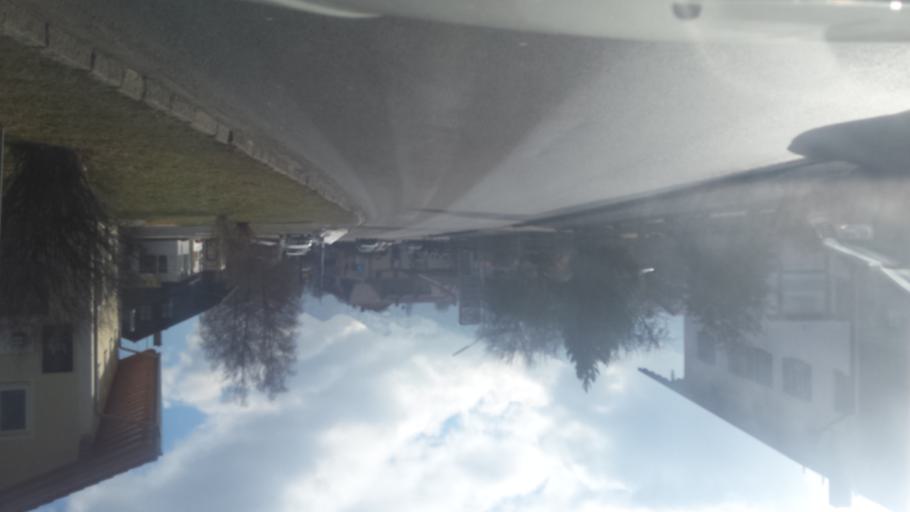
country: DE
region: Bavaria
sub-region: Upper Bavaria
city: Kochel
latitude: 47.6609
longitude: 11.3731
